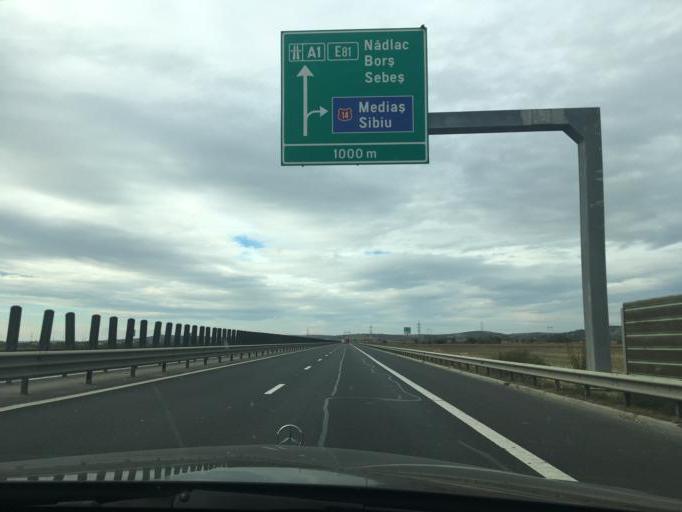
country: RO
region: Sibiu
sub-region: Municipiul Sibiu
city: Sibiu
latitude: 45.8119
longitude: 24.1708
